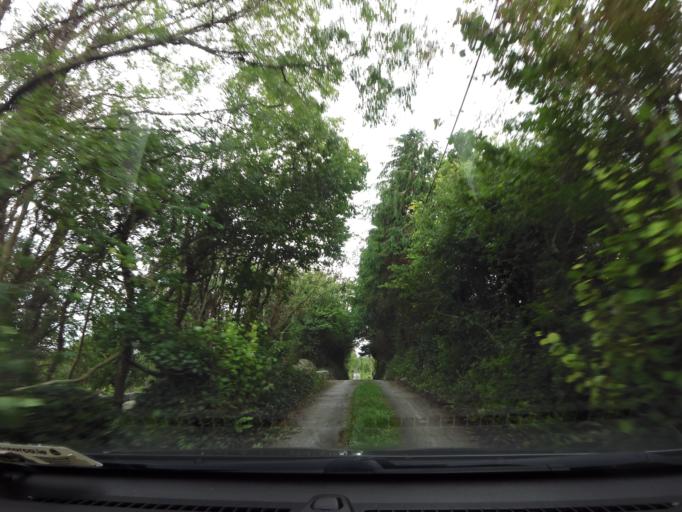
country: IE
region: Connaught
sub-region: County Galway
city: Moycullen
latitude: 53.3343
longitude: -9.1397
